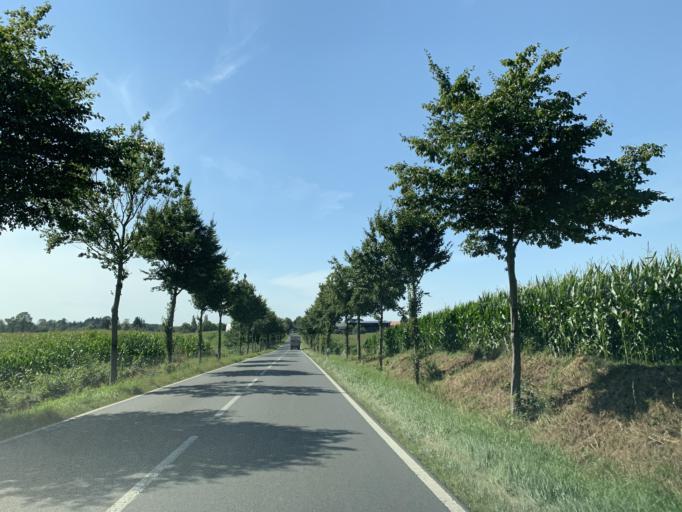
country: DE
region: Mecklenburg-Vorpommern
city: Loitz
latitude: 53.3366
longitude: 13.3928
